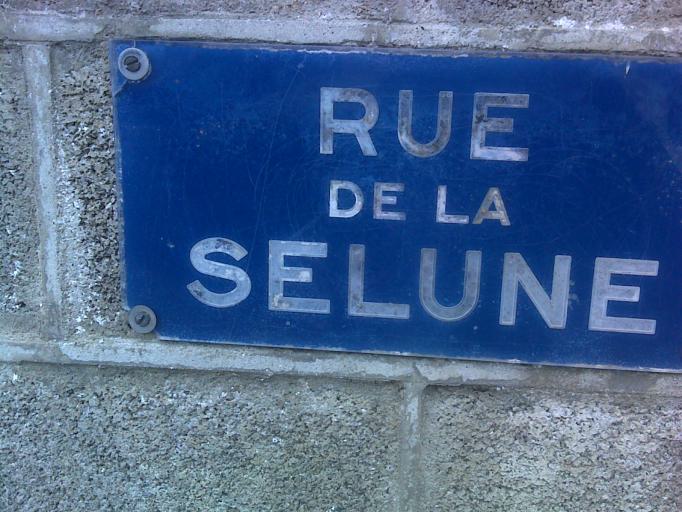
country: FR
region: Lower Normandy
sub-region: Departement de la Manche
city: Saint-Quentin-sur-le-Homme
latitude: 48.6305
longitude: -1.3504
